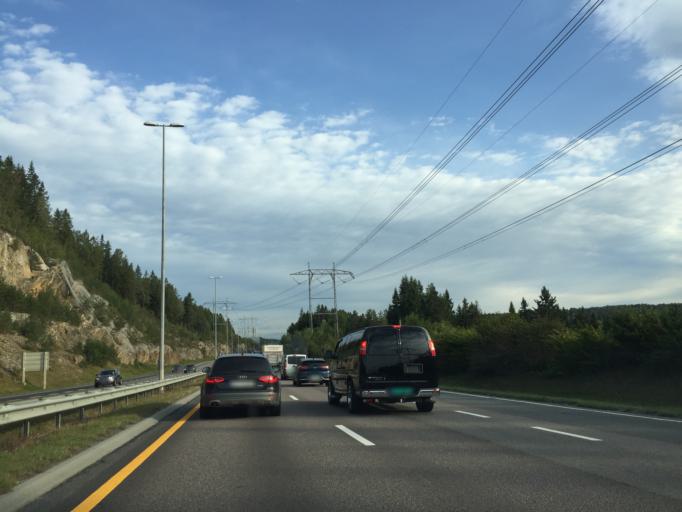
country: NO
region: Akershus
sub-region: Oppegard
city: Kolbotn
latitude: 59.8217
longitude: 10.8462
